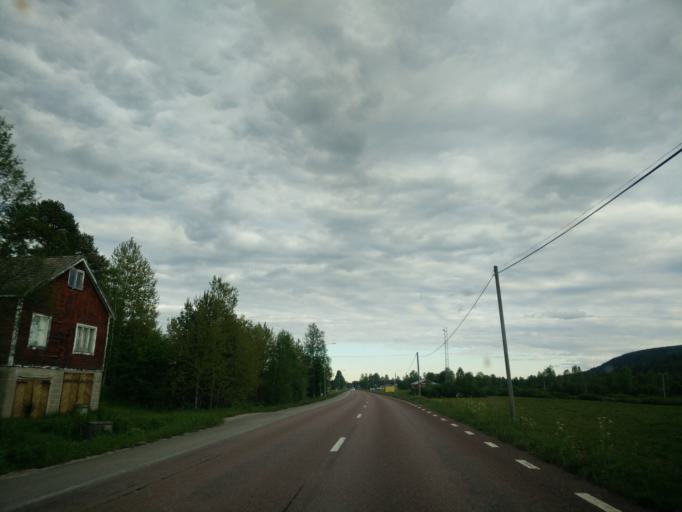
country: SE
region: Jaemtland
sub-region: Harjedalens Kommun
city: Sveg
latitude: 62.2874
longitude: 14.7959
